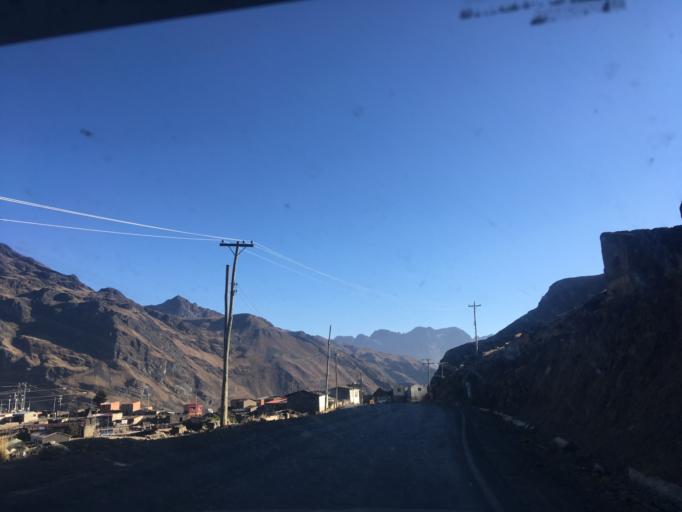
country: BO
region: La Paz
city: Quime
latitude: -17.0351
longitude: -67.2830
